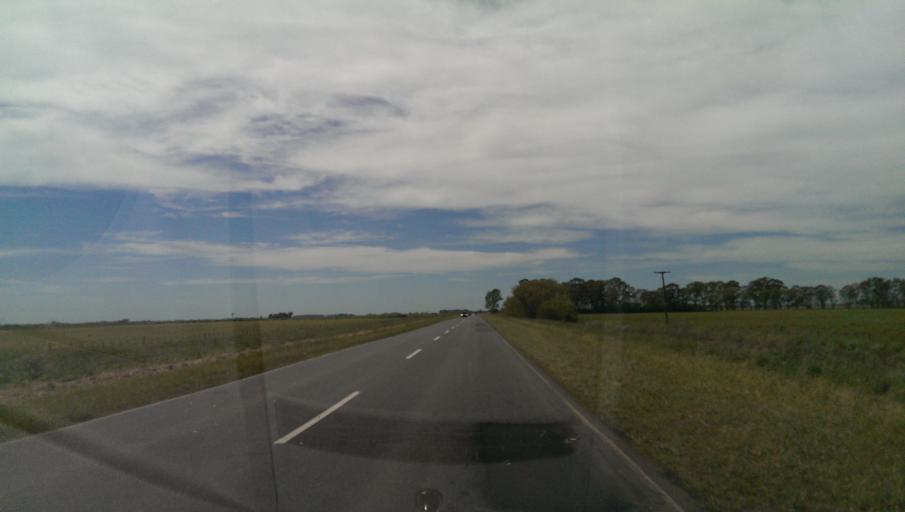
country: AR
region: Buenos Aires
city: Olavarria
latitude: -37.0203
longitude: -60.4122
